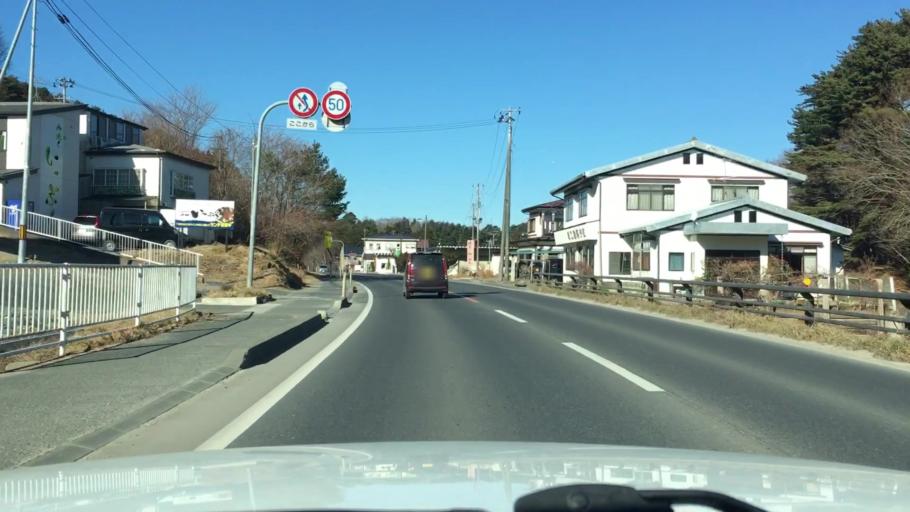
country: JP
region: Iwate
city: Yamada
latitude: 39.4427
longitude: 141.9715
